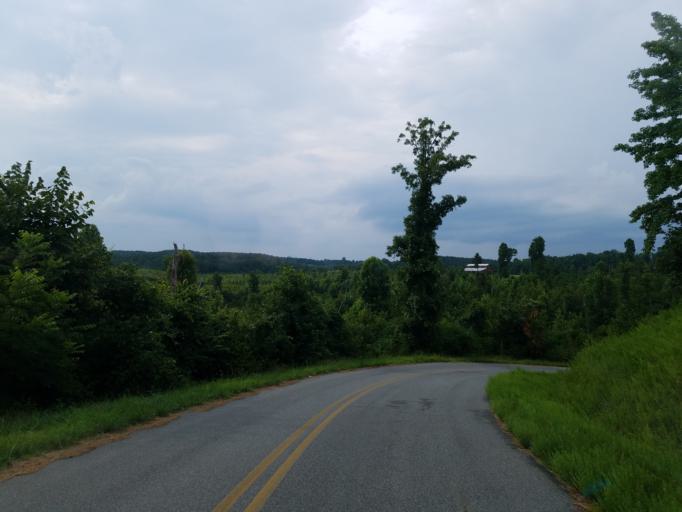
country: US
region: Georgia
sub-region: Bartow County
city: Rydal
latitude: 34.3897
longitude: -84.6701
